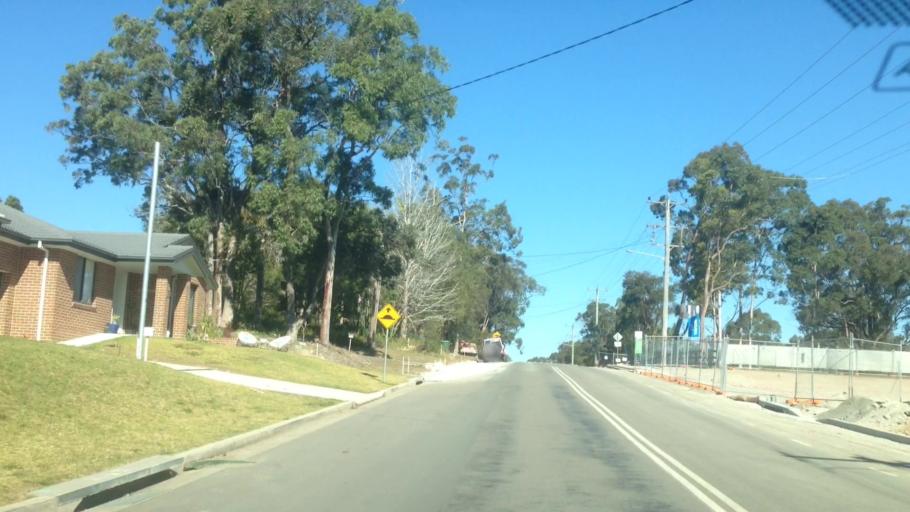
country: AU
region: New South Wales
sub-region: Lake Macquarie Shire
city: Cooranbong
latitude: -33.0921
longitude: 151.4508
